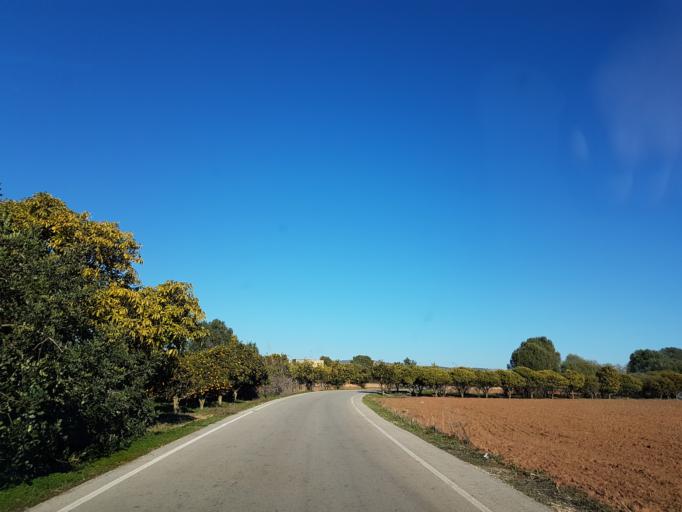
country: PT
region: Faro
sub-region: Loule
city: Boliqueime
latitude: 37.1008
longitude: -8.1609
